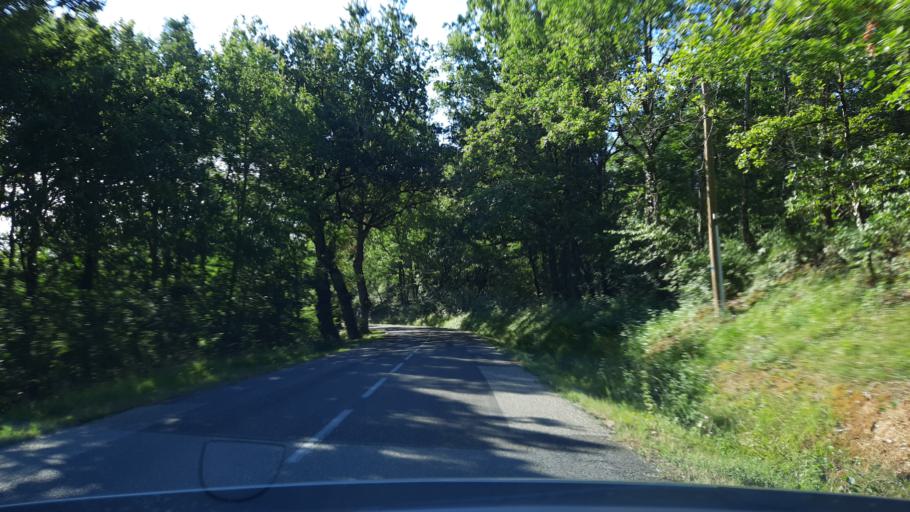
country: FR
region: Midi-Pyrenees
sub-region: Departement du Tarn-et-Garonne
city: Molieres
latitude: 44.1857
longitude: 1.3461
